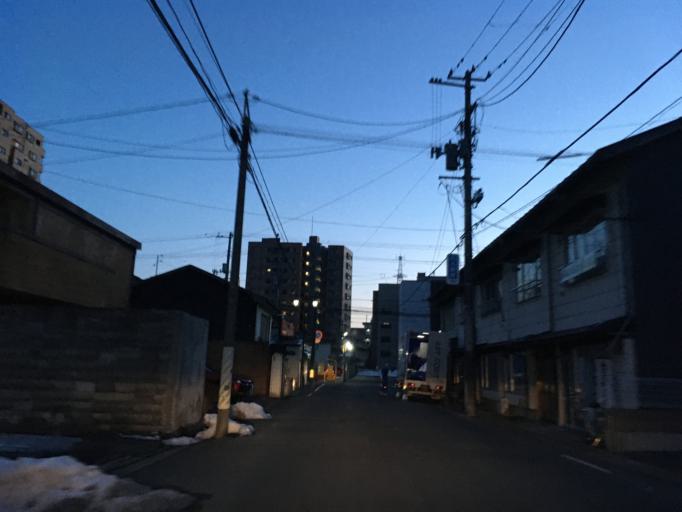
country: JP
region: Iwate
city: Morioka-shi
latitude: 39.7063
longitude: 141.1545
